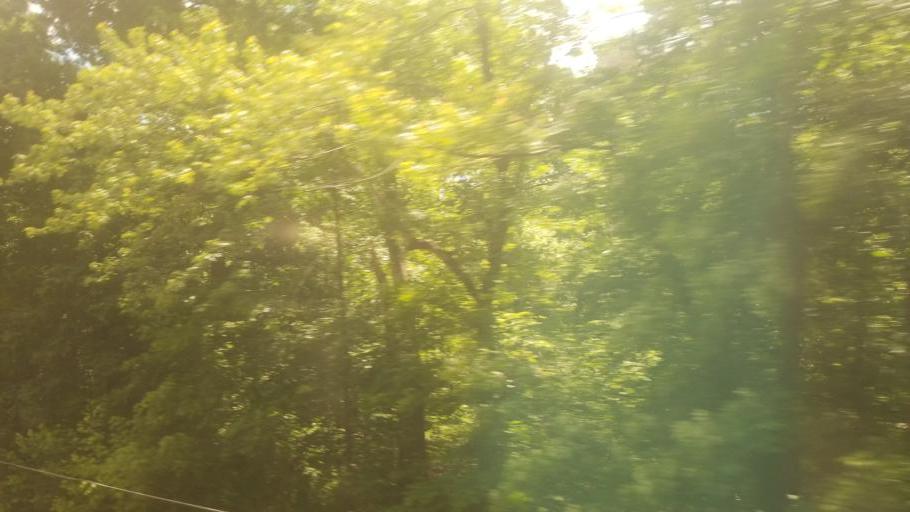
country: US
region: Maryland
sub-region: Frederick County
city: Brunswick
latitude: 39.3156
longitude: -77.6461
